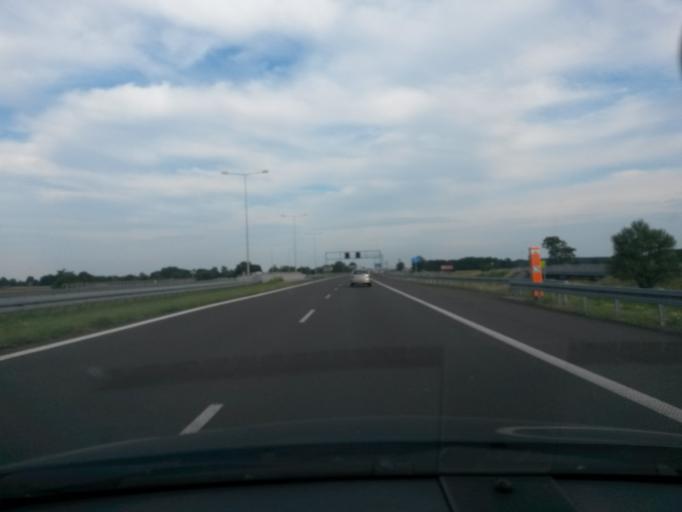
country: PL
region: Greater Poland Voivodeship
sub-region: Powiat turecki
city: Brudzew
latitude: 52.1395
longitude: 18.6144
